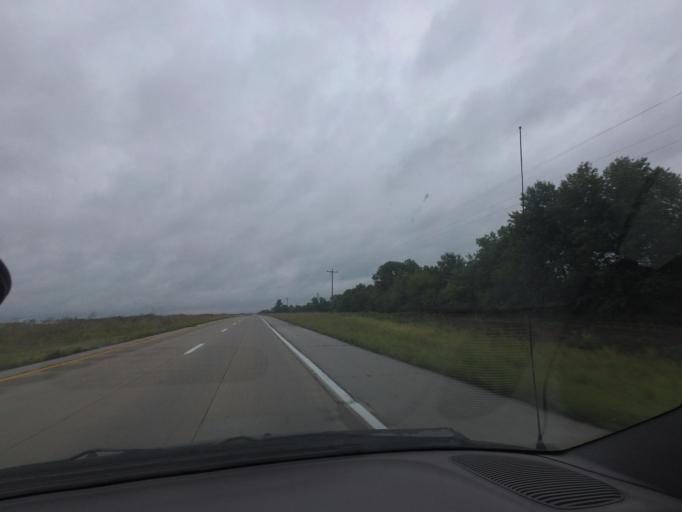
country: US
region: Missouri
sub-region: Marion County
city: Monroe City
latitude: 39.6583
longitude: -91.8056
